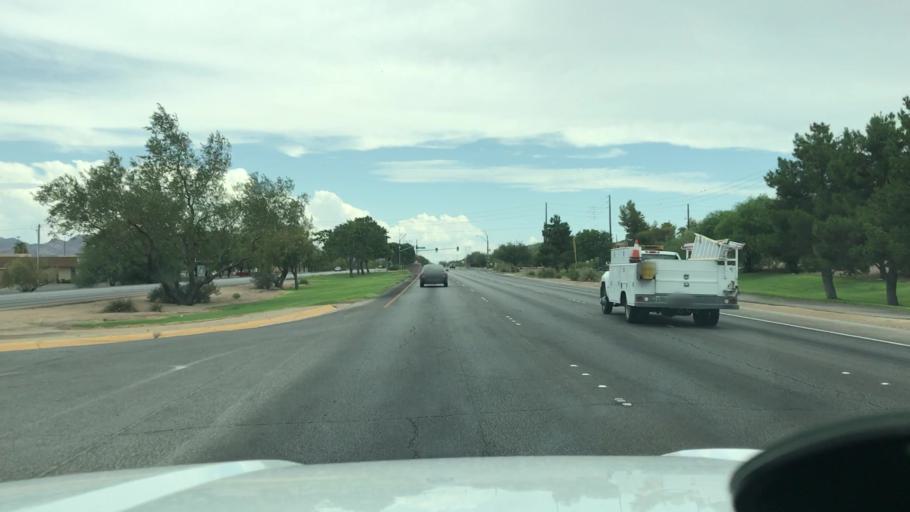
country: US
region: Nevada
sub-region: Clark County
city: Henderson
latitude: 36.0315
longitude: -114.9731
